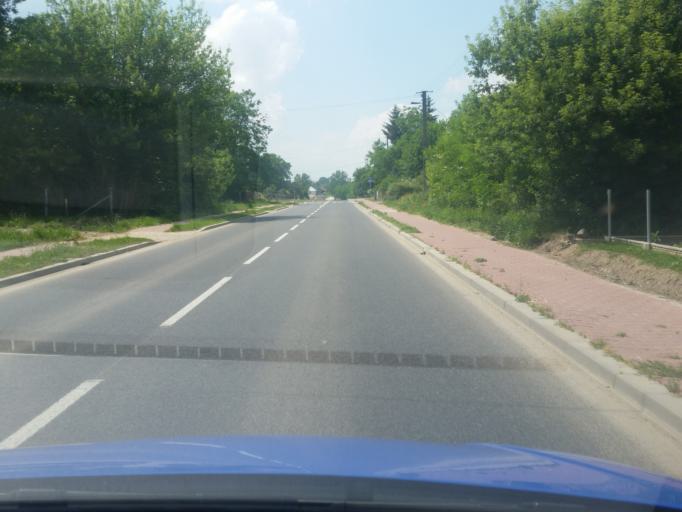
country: PL
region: Swietokrzyskie
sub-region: Powiat pinczowski
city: Zlota
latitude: 50.3382
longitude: 20.6144
